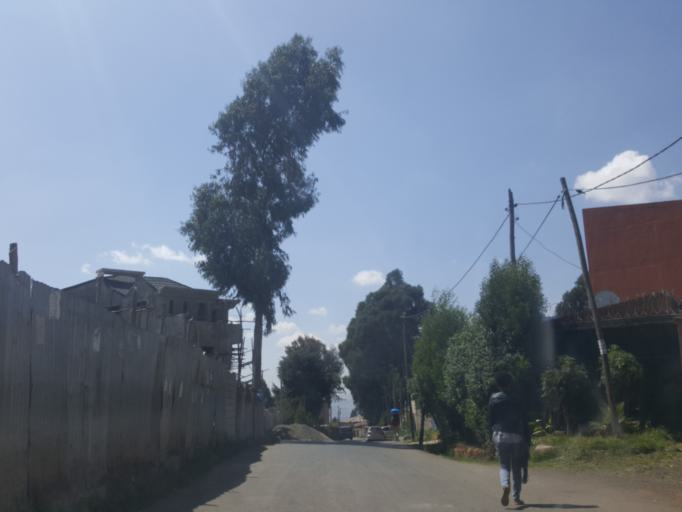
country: ET
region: Adis Abeba
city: Addis Ababa
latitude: 9.0599
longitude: 38.7332
